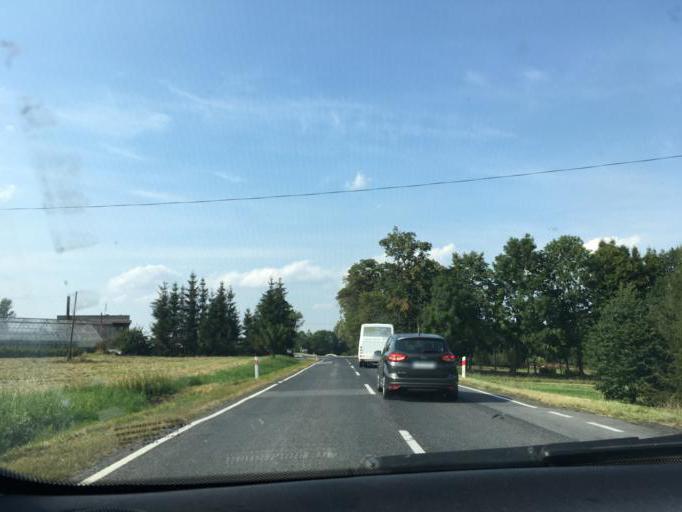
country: PL
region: Opole Voivodeship
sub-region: Powiat prudnicki
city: Laka Prudnicka
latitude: 50.3737
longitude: 17.5355
